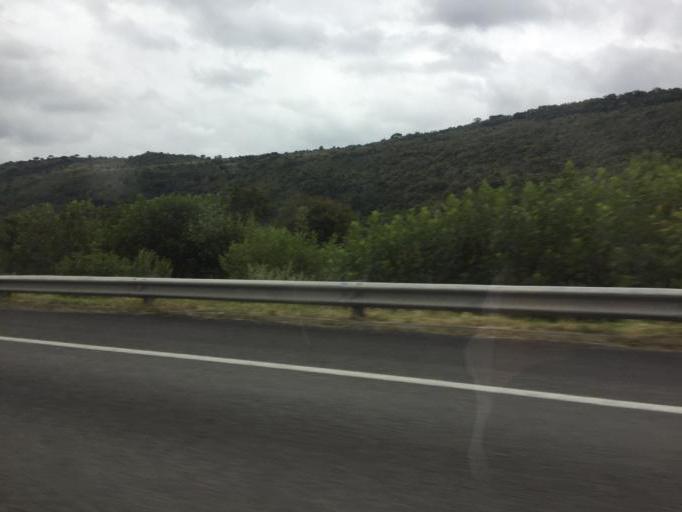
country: MX
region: Jalisco
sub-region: Zapotlan del Rey
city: Zapotlan del Rey
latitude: 20.5236
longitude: -102.9968
